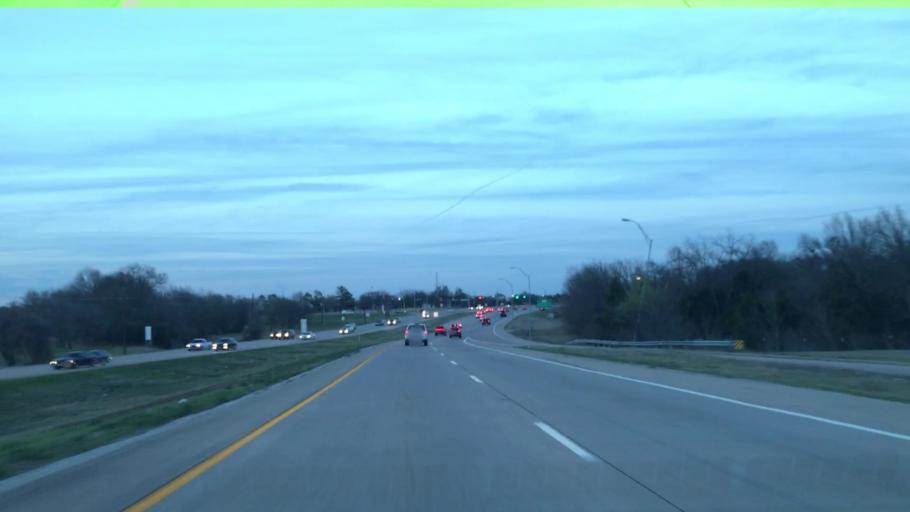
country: US
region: Texas
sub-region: Dallas County
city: Coppell
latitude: 32.9918
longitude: -97.0067
